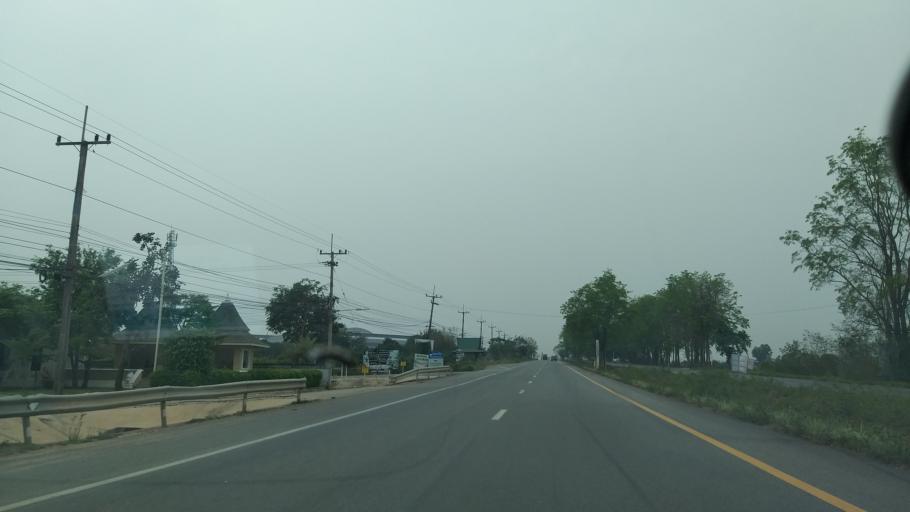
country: TH
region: Chachoengsao
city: Plaeng Yao
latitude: 13.5013
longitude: 101.2711
